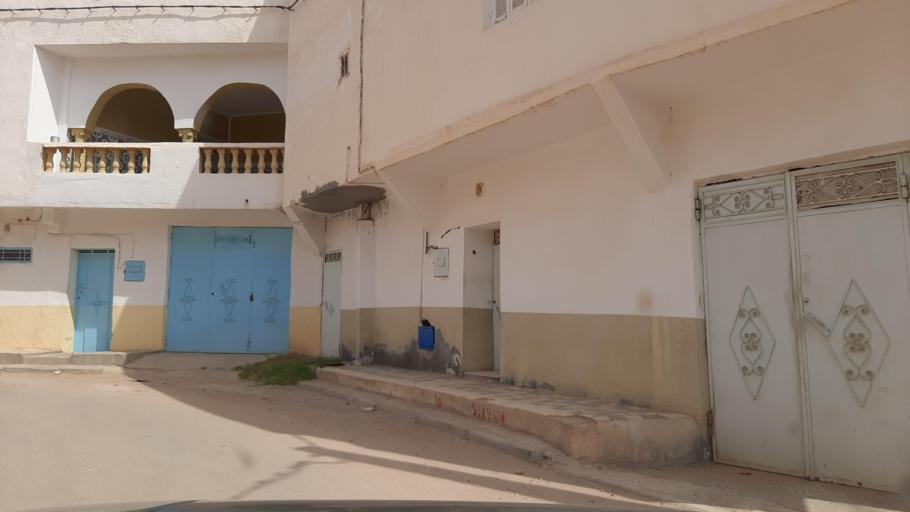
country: TN
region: Tataouine
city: Tataouine
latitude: 32.9318
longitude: 10.4548
